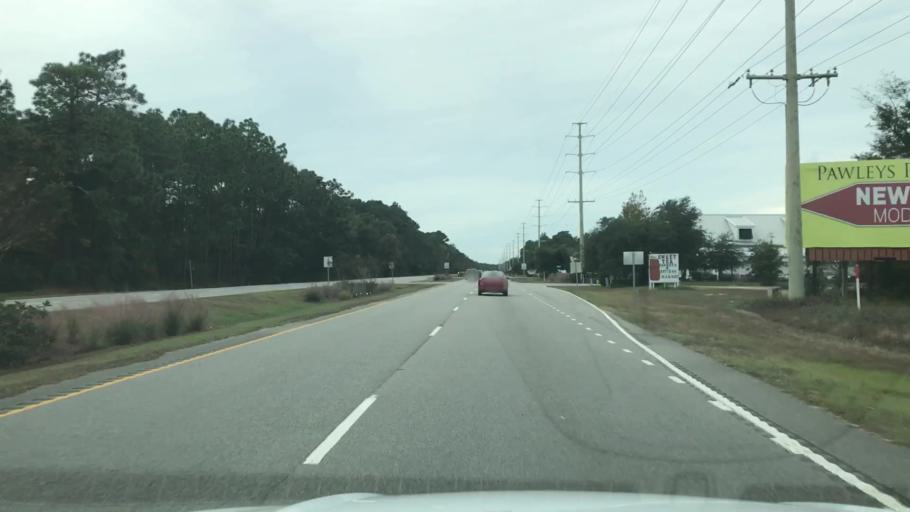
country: US
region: South Carolina
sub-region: Georgetown County
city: Georgetown
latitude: 33.4253
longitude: -79.1593
